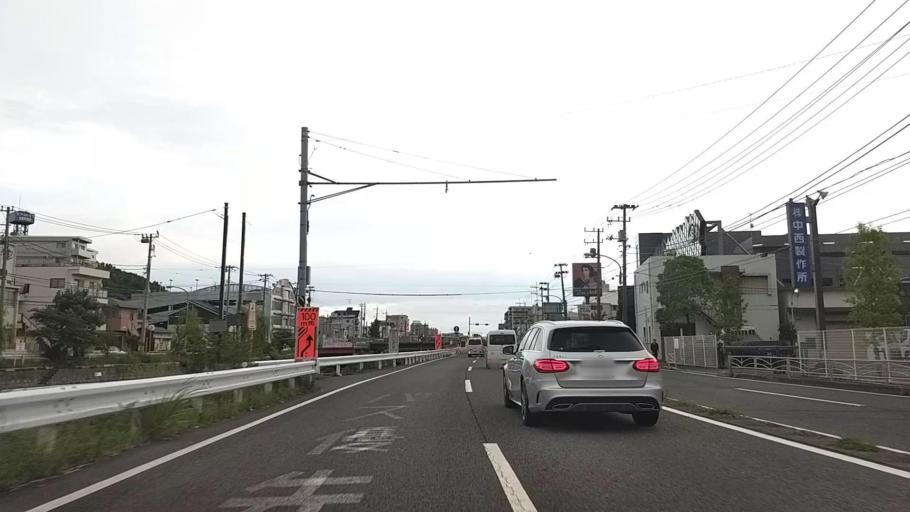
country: JP
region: Kanagawa
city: Yokohama
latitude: 35.4276
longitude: 139.6225
